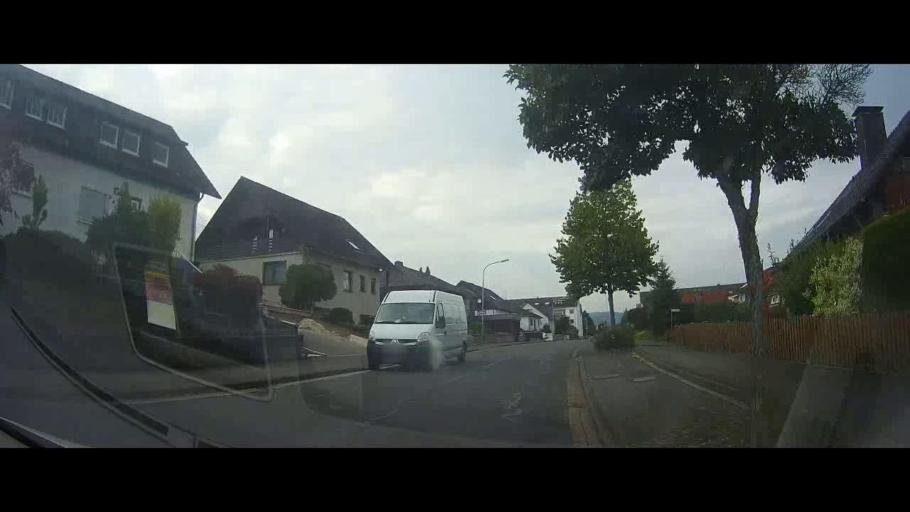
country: DE
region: Lower Saxony
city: Uslar
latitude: 51.6322
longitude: 9.6590
